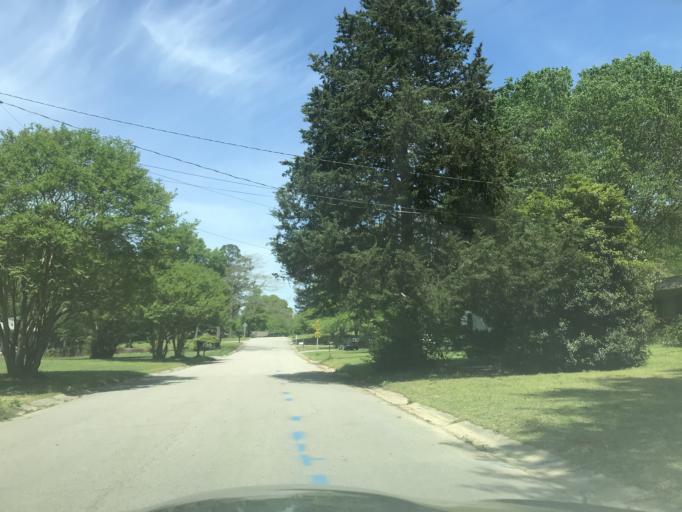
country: US
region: North Carolina
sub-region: Wake County
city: Raleigh
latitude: 35.8314
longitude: -78.5809
